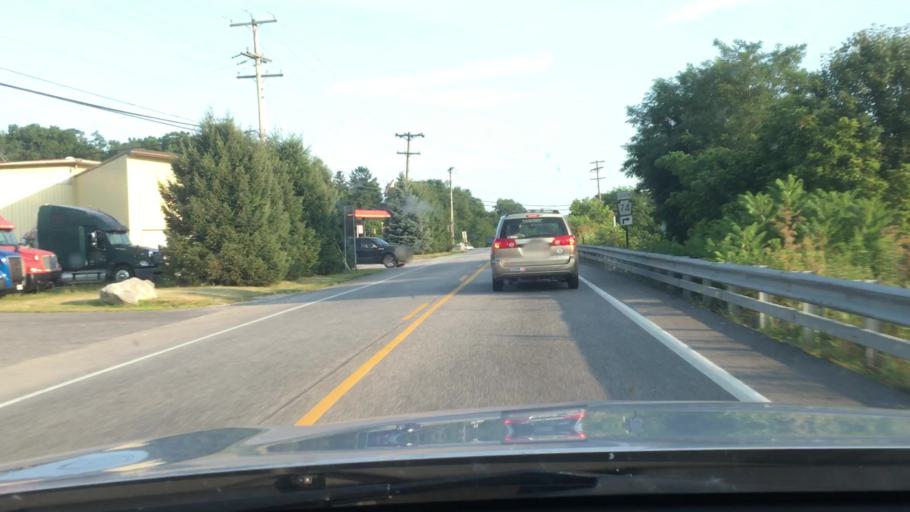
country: US
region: Pennsylvania
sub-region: York County
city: Dillsburg
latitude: 40.1213
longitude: -77.0359
